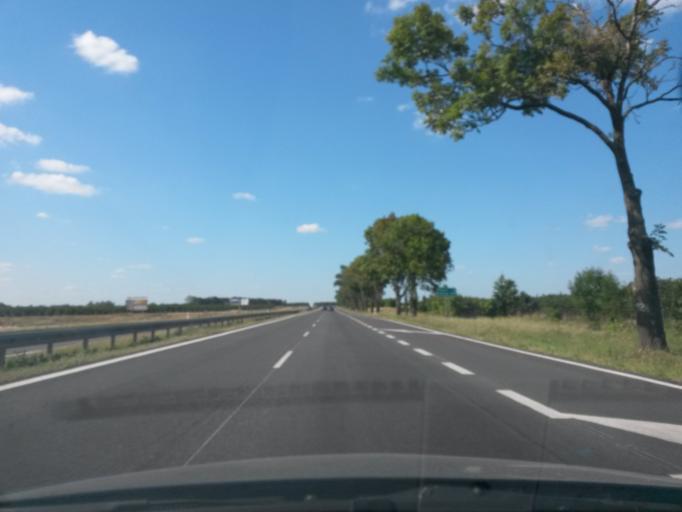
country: PL
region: Masovian Voivodeship
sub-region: Powiat plonski
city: Zaluski
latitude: 52.5704
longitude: 20.4854
